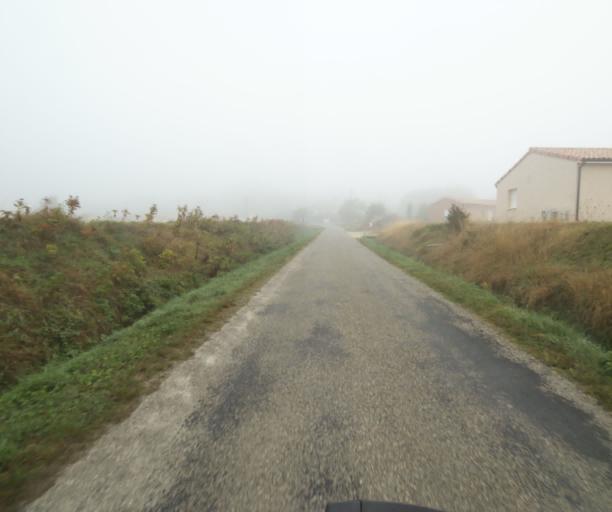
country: FR
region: Midi-Pyrenees
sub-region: Departement de la Haute-Garonne
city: Villemur-sur-Tarn
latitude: 43.9127
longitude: 1.4827
